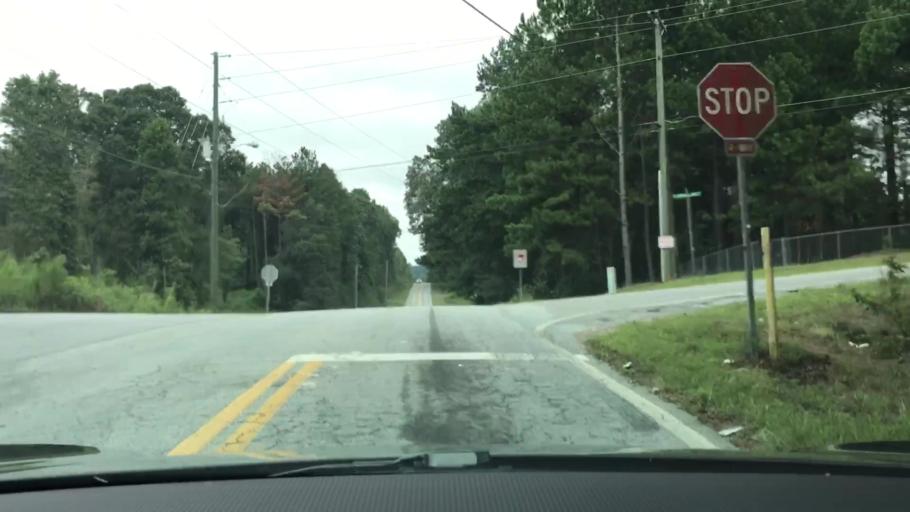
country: US
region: Georgia
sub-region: Barrow County
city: Auburn
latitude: 34.0507
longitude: -83.8173
